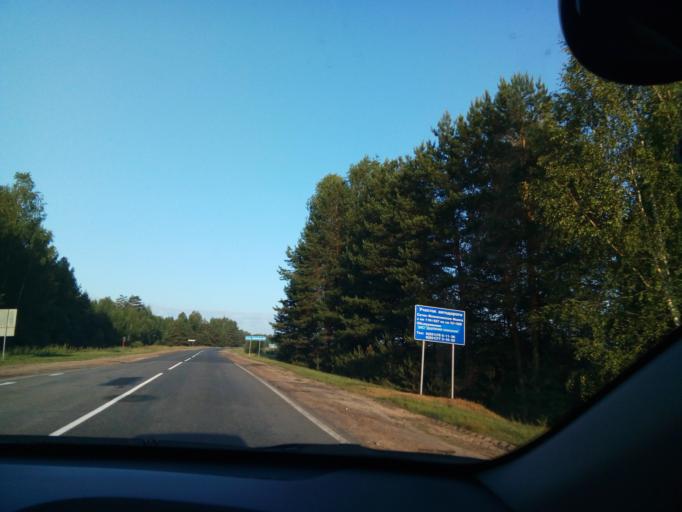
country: RU
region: Nizjnij Novgorod
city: Satis
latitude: 54.9319
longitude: 43.2136
